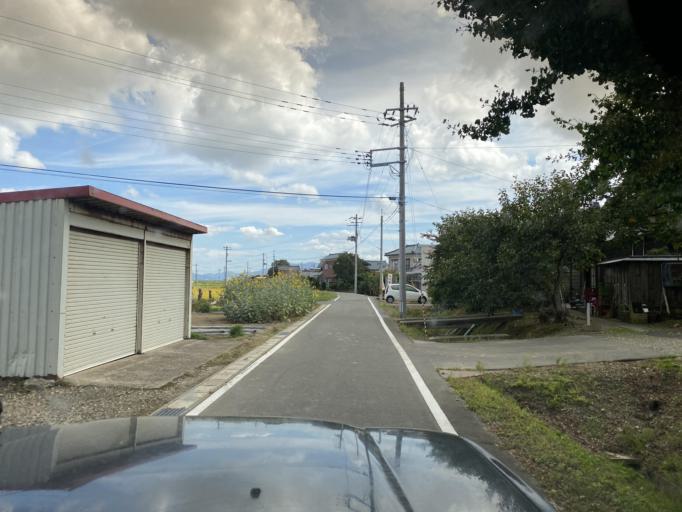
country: JP
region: Niigata
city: Niitsu-honcho
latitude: 37.8179
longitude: 139.0782
